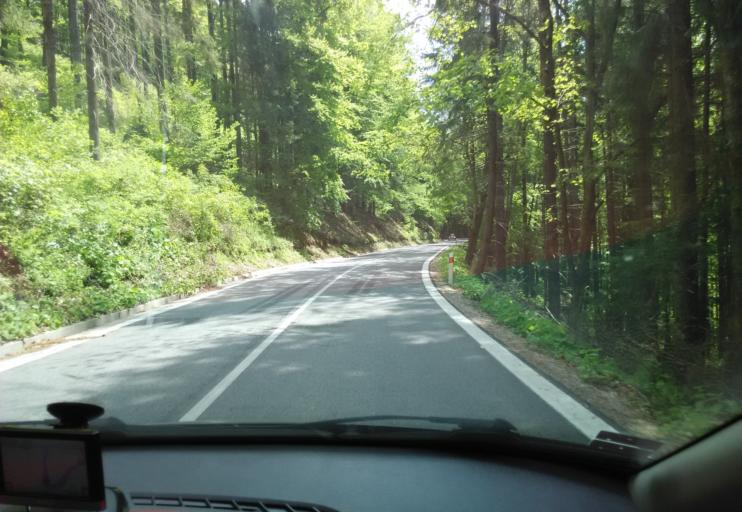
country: SK
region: Kosicky
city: Dobsina
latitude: 48.8550
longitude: 20.4617
